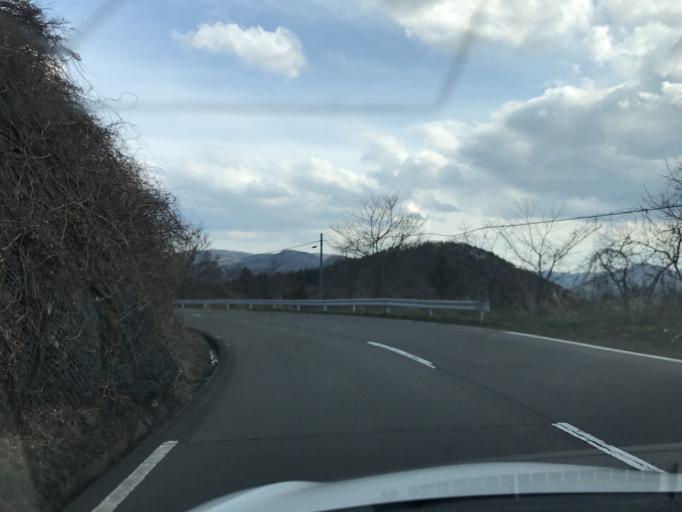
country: JP
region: Miyagi
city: Shiroishi
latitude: 38.0223
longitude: 140.5649
